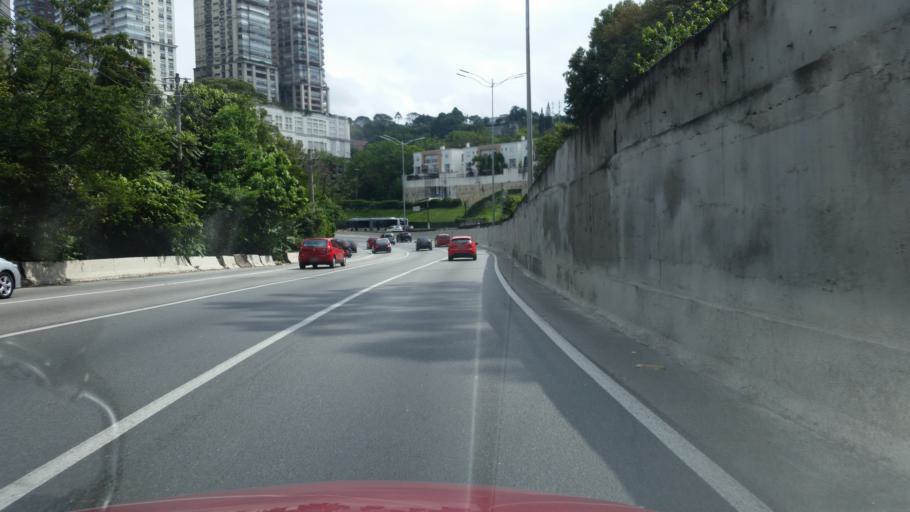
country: BR
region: Sao Paulo
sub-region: Sao Paulo
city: Sao Paulo
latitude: -23.5957
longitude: -46.6960
